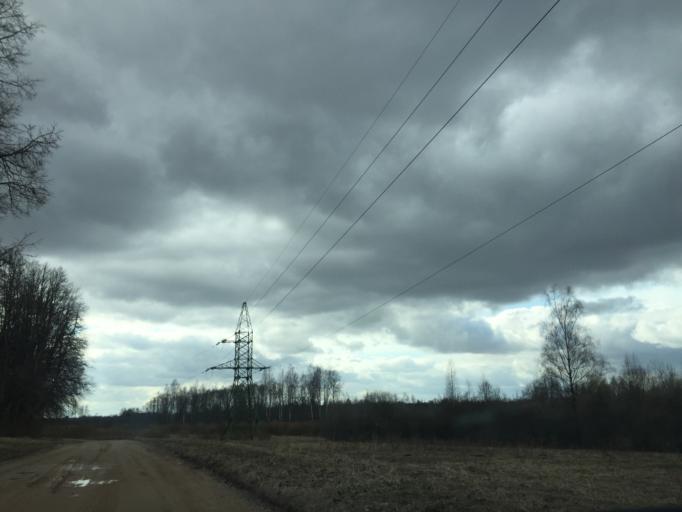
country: LV
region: Vecumnieki
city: Vecumnieki
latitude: 56.5759
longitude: 24.6018
